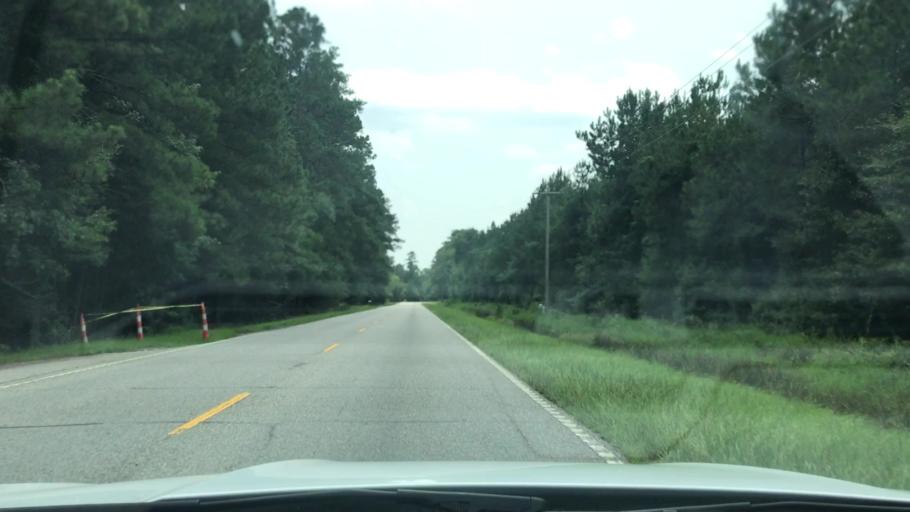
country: US
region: South Carolina
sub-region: Georgetown County
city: Murrells Inlet
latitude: 33.6240
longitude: -79.1915
